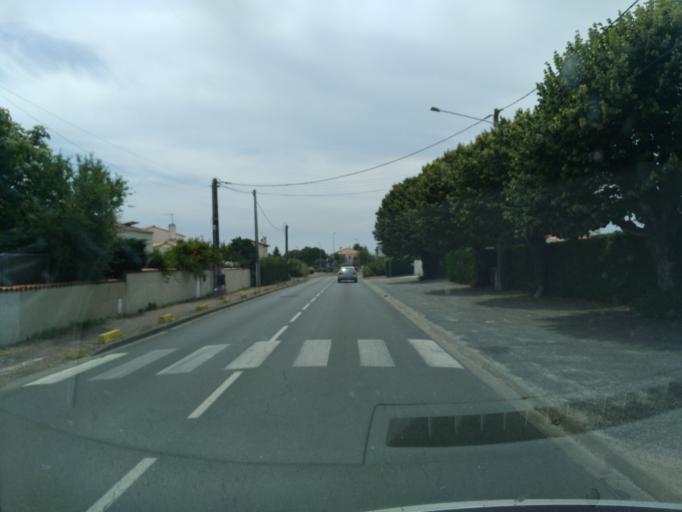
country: FR
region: Poitou-Charentes
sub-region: Departement de la Charente-Maritime
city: Saint-Palais-sur-Mer
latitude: 45.6514
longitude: -1.0805
